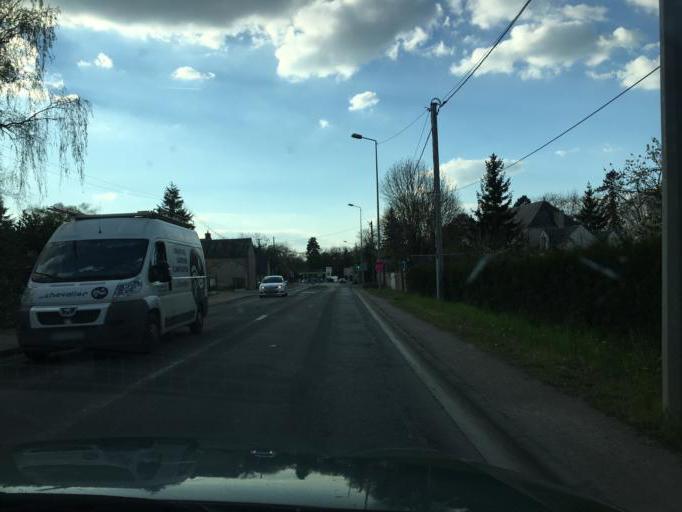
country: FR
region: Centre
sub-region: Departement du Loiret
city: Saint-Jean-le-Blanc
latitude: 47.8791
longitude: 1.9367
